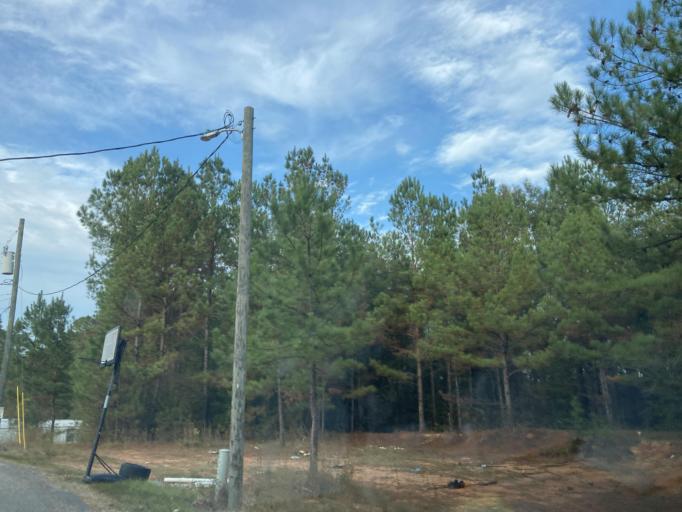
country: US
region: Mississippi
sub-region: Lamar County
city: Purvis
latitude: 31.2048
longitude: -89.3574
